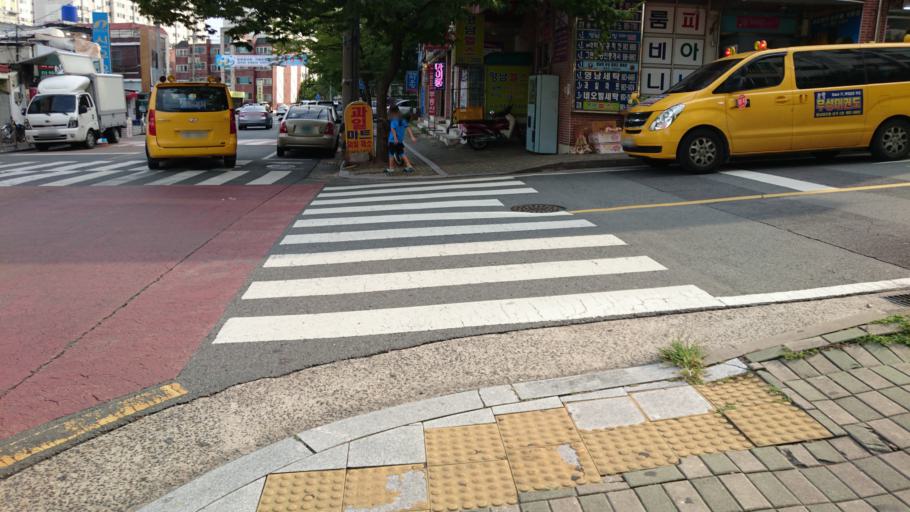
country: KR
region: Daegu
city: Daegu
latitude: 35.8812
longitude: 128.6617
